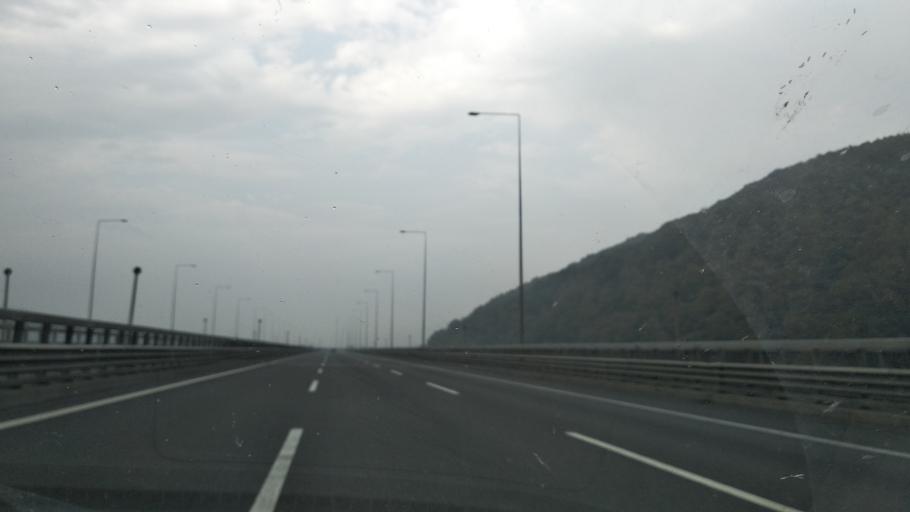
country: TR
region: Duzce
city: Kaynasli
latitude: 40.7682
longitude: 31.3719
